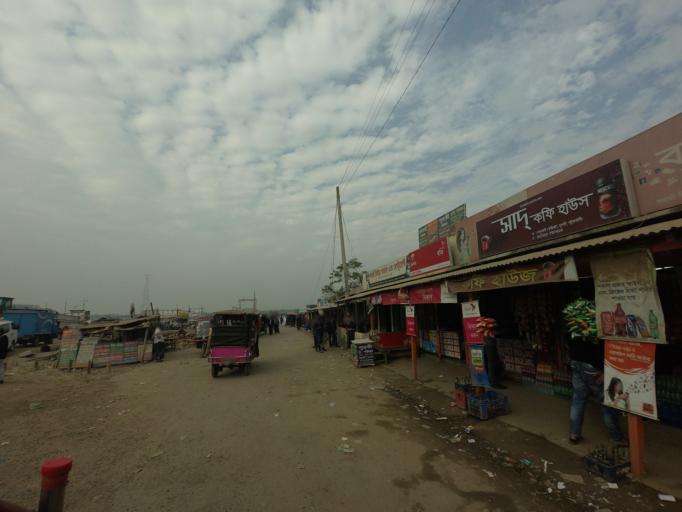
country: BD
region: Barisal
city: Nalchiti
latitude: 22.4630
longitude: 90.3416
